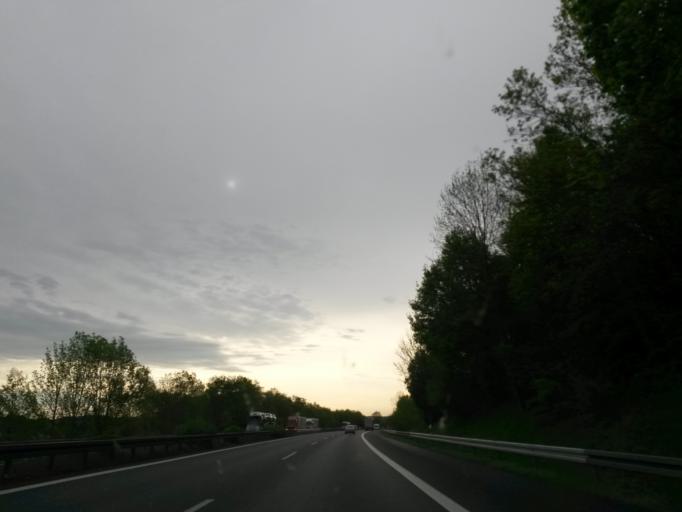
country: DE
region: Bavaria
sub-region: Upper Franconia
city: Schlusselfeld
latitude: 49.7595
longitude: 10.5972
